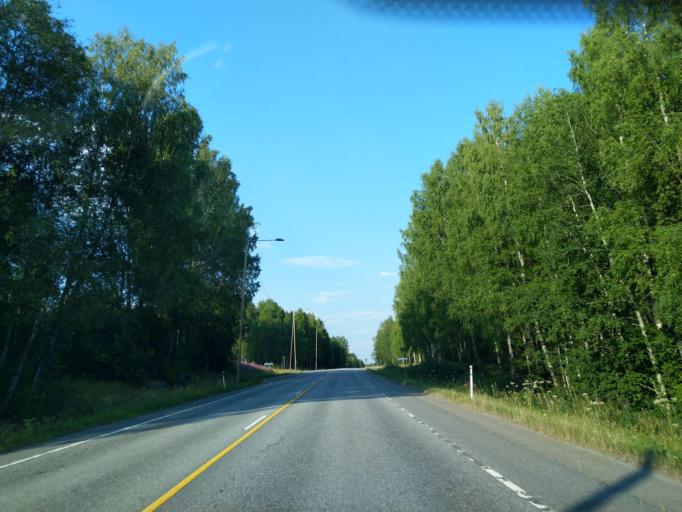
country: FI
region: Satakunta
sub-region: Pori
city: Laengelmaeki
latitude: 61.7491
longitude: 22.1084
